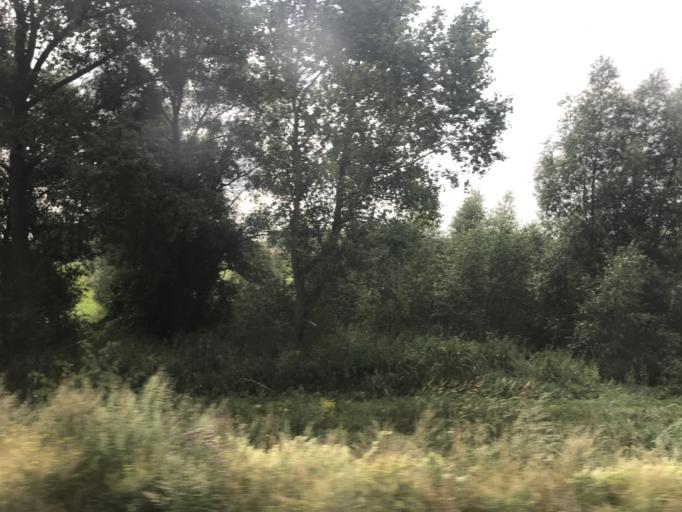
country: PL
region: Greater Poland Voivodeship
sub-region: Powiat gnieznienski
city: Lubowo
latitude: 52.5023
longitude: 17.4550
